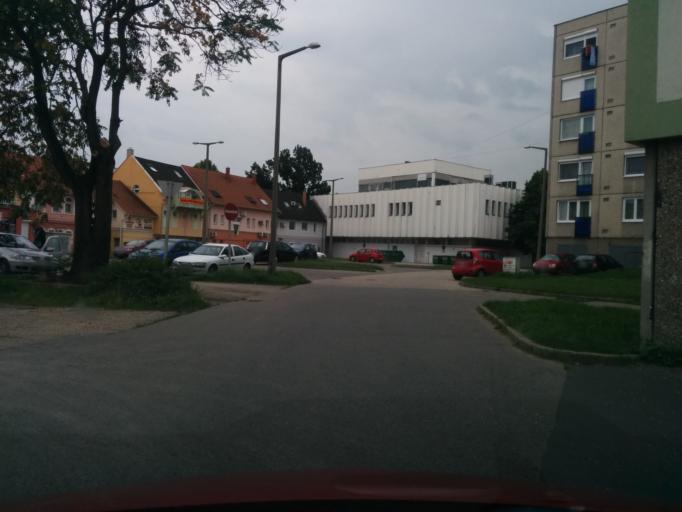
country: HU
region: Komarom-Esztergom
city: Komarom
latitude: 47.7447
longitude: 18.1183
